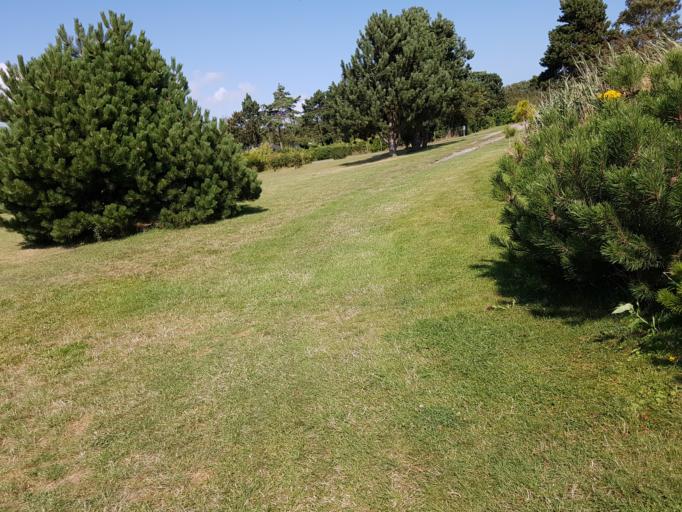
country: DK
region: Zealand
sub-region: Guldborgsund Kommune
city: Nykobing Falster
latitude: 54.5889
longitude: 11.9618
